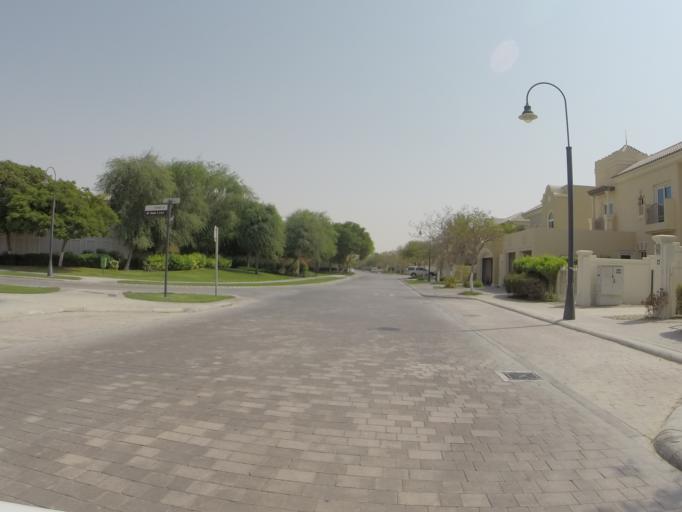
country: AE
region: Dubai
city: Dubai
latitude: 25.0367
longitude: 55.2165
